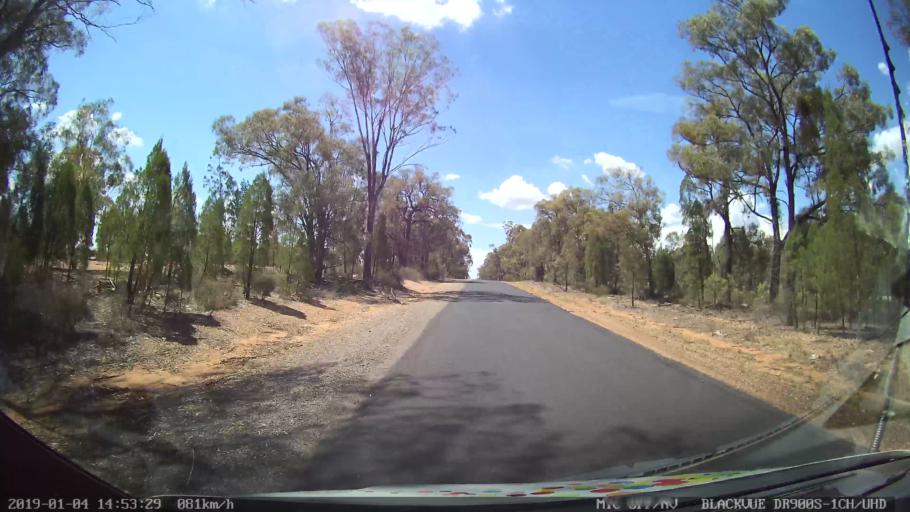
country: AU
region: New South Wales
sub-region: Dubbo Municipality
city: Dubbo
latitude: -32.0026
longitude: 148.6520
